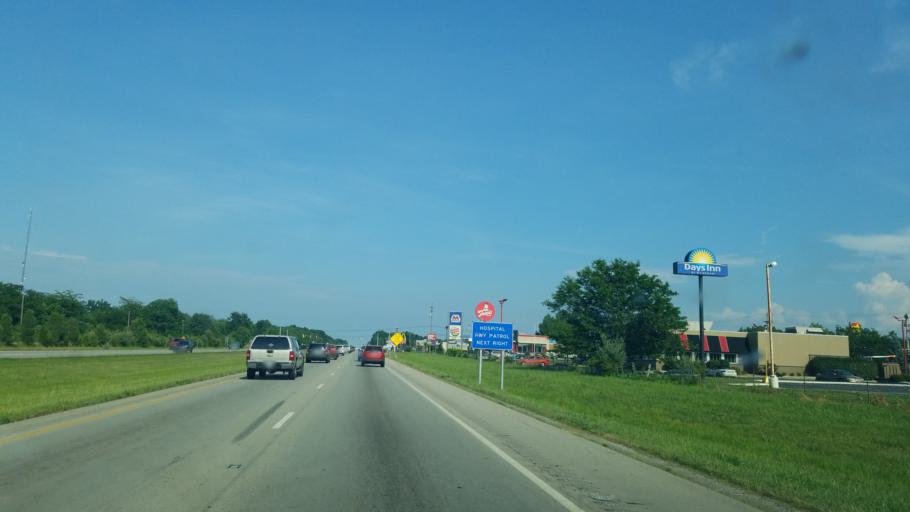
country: US
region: Ohio
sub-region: Clermont County
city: Batavia
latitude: 39.0842
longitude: -84.1543
